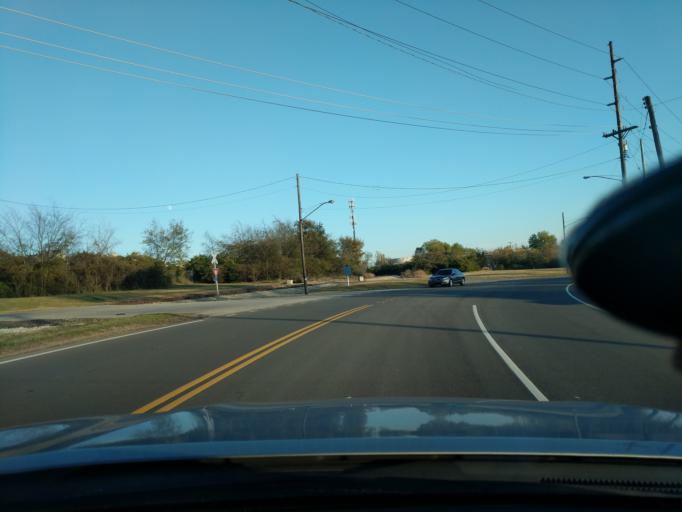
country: US
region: Tennessee
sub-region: Davidson County
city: Belle Meade
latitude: 36.1716
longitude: -86.8633
